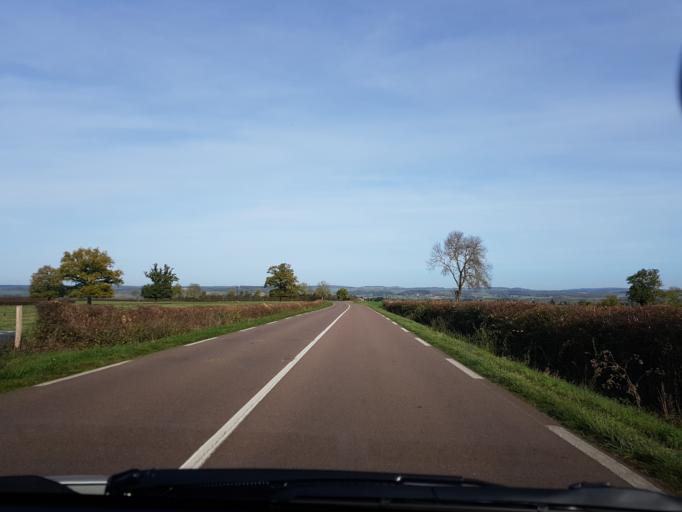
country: FR
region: Bourgogne
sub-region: Departement de l'Yonne
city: Avallon
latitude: 47.4829
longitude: 4.0604
